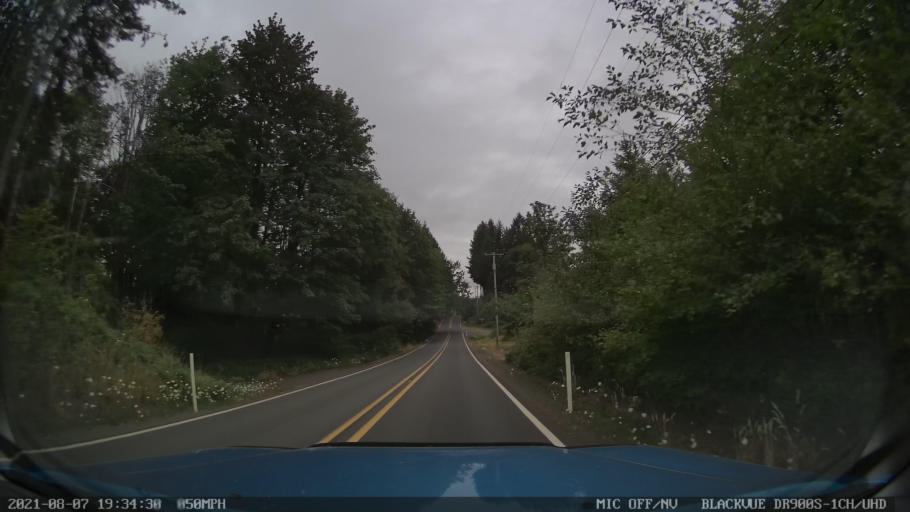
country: US
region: Oregon
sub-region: Linn County
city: Lyons
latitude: 44.9183
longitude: -122.6558
